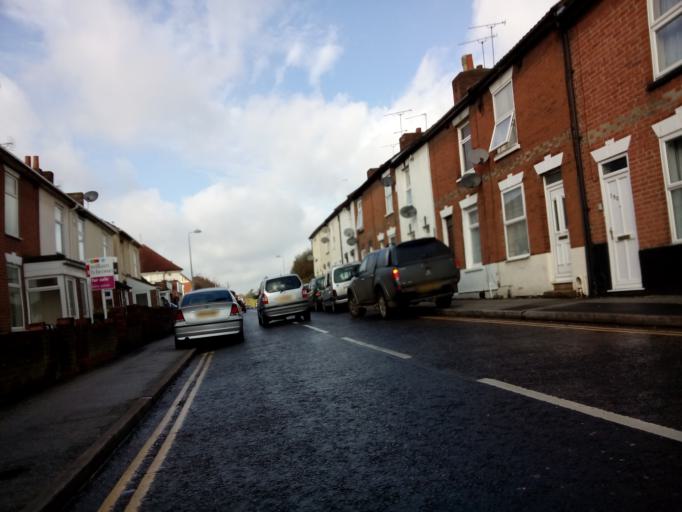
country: GB
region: England
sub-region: Suffolk
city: Ipswich
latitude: 52.0667
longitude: 1.1333
